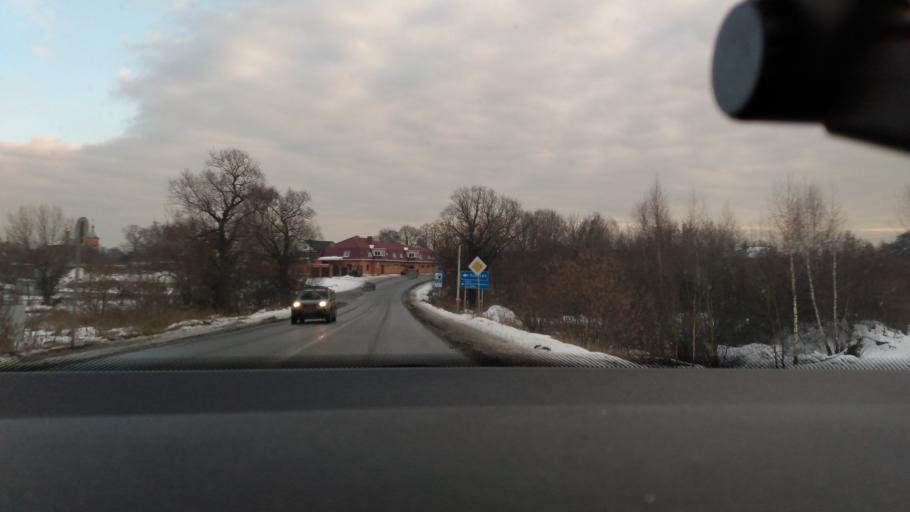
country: RU
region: Moskovskaya
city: Chornaya
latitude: 55.7112
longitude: 38.0475
